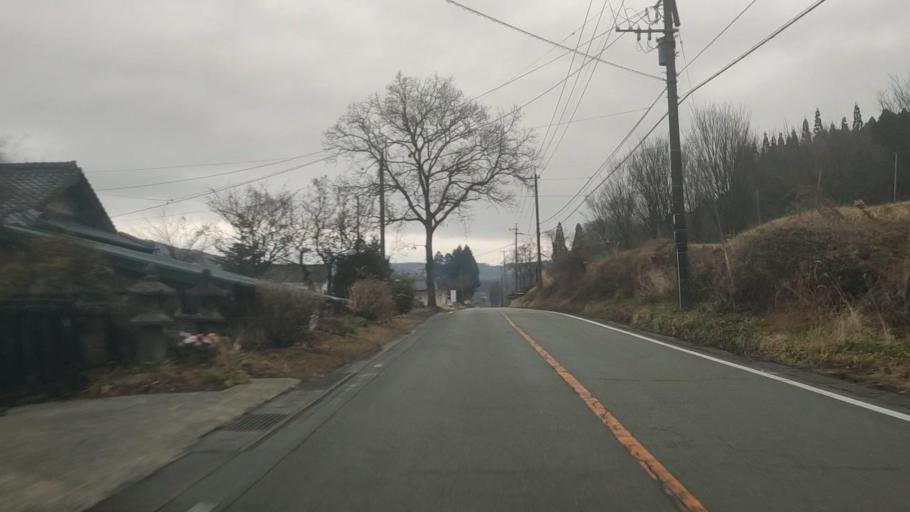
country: JP
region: Kumamoto
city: Aso
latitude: 32.8520
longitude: 131.1519
